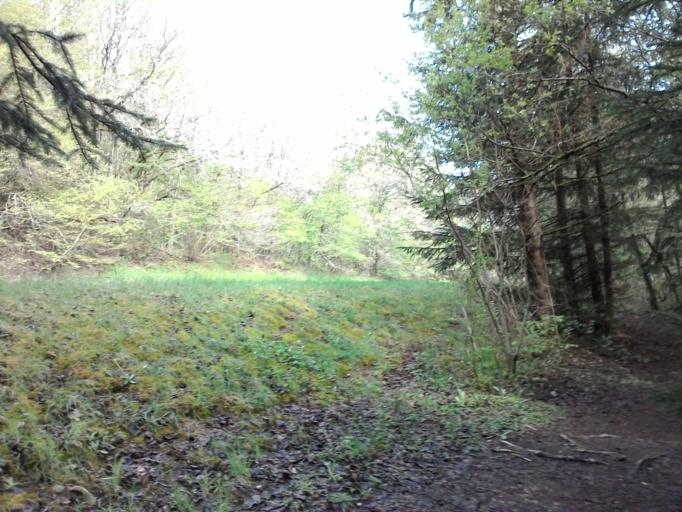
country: FR
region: Bourgogne
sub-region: Departement de la Cote-d'Or
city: Saulieu
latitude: 47.2484
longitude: 4.1877
